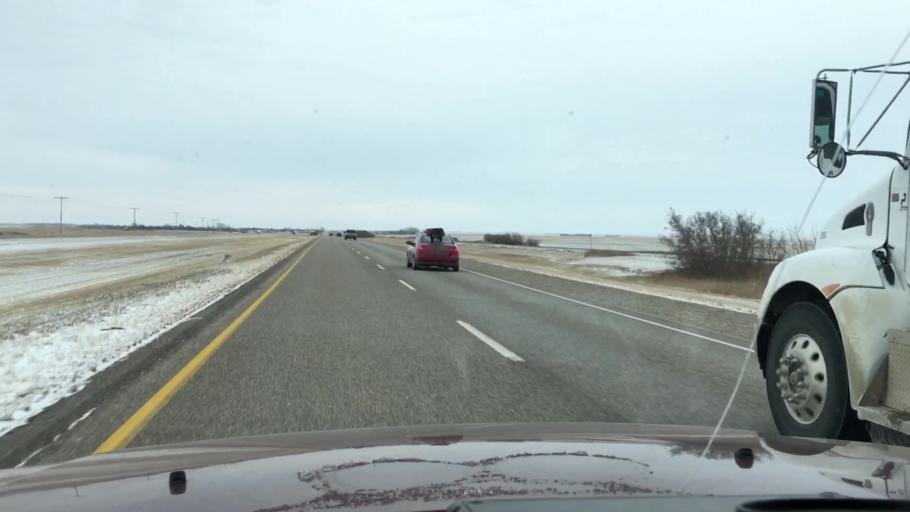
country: CA
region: Saskatchewan
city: Watrous
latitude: 51.1768
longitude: -105.9360
